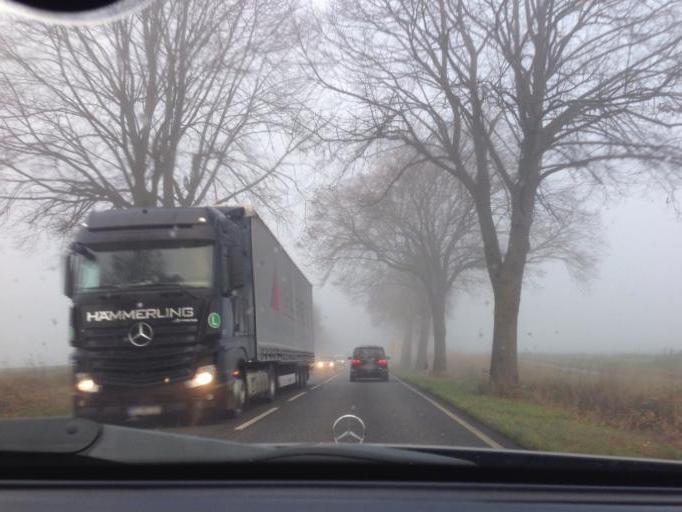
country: DE
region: Schleswig-Holstein
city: Stapelfeld
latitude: 53.6401
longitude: 10.1951
